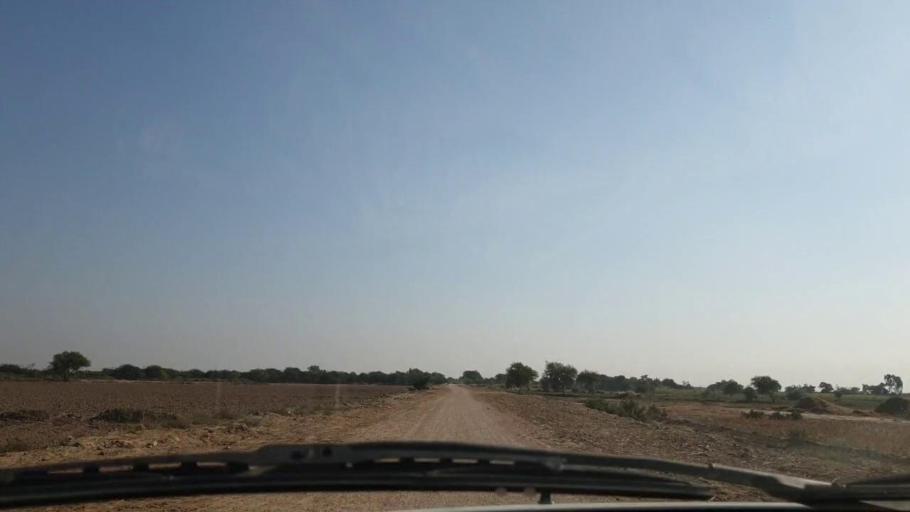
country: PK
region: Sindh
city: Bulri
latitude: 24.7984
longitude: 68.3941
